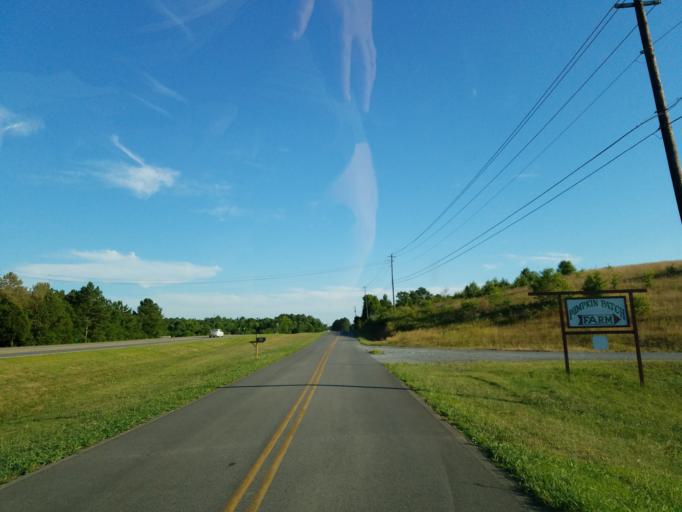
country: US
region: Georgia
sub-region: Bartow County
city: Adairsville
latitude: 34.3897
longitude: -84.9346
